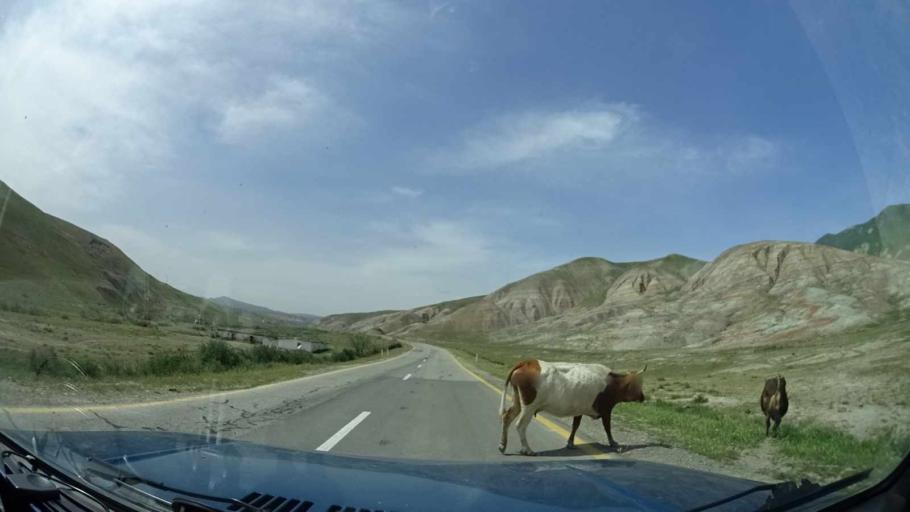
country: AZ
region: Xizi
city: Khyzy
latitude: 40.8751
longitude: 49.1975
